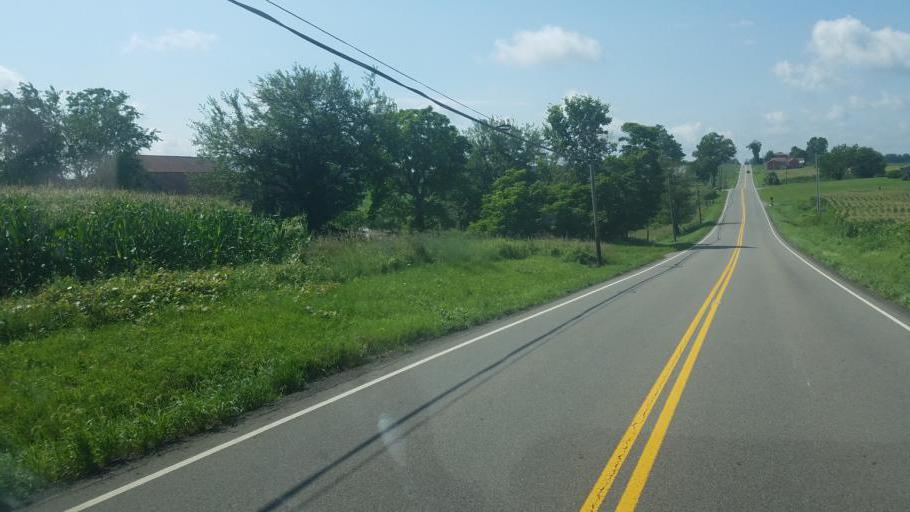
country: US
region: Ohio
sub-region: Licking County
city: Granville
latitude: 40.1059
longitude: -82.5189
